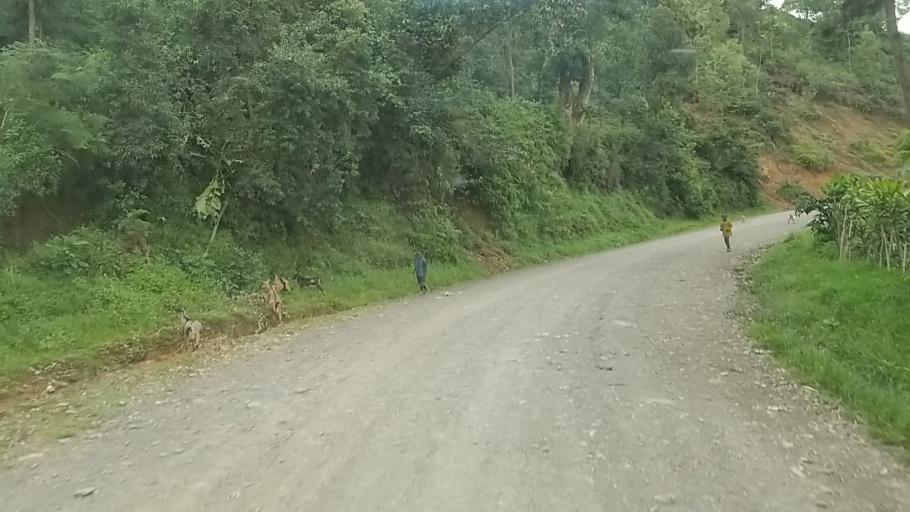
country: CD
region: Nord Kivu
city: Sake
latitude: -1.9245
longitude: 28.9449
